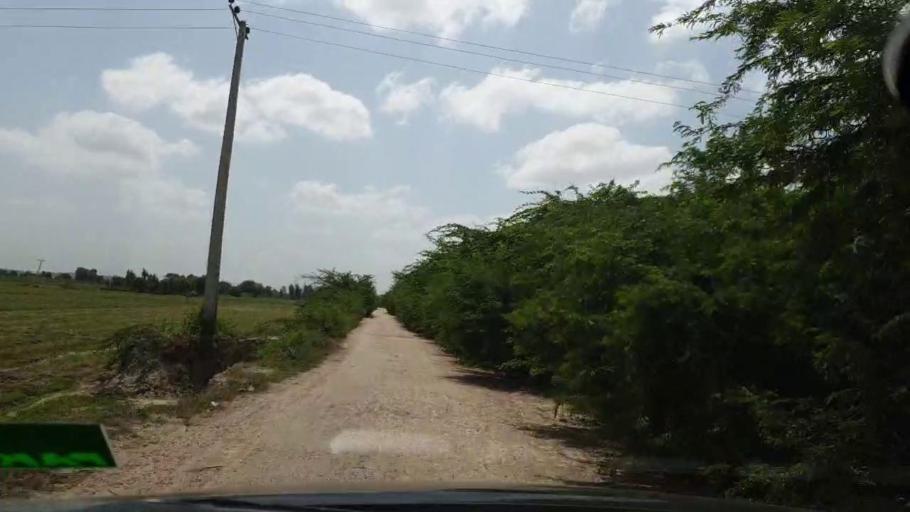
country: PK
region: Sindh
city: Kadhan
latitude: 24.5656
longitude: 69.2110
